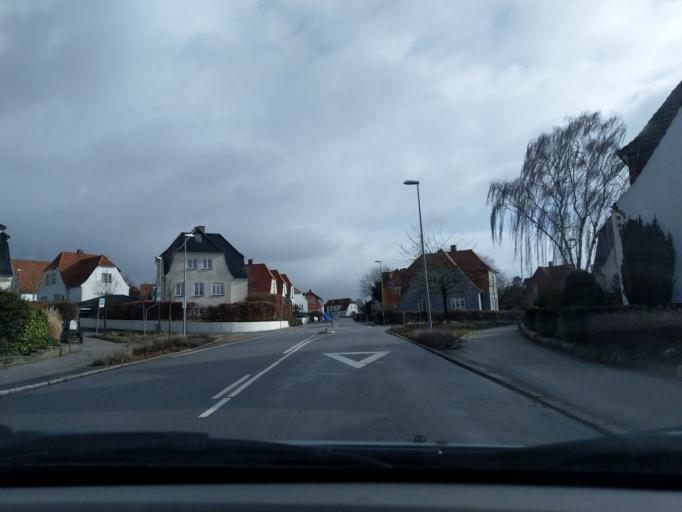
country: DK
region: Zealand
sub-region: Naestved Kommune
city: Naestved
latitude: 55.2242
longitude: 11.7658
